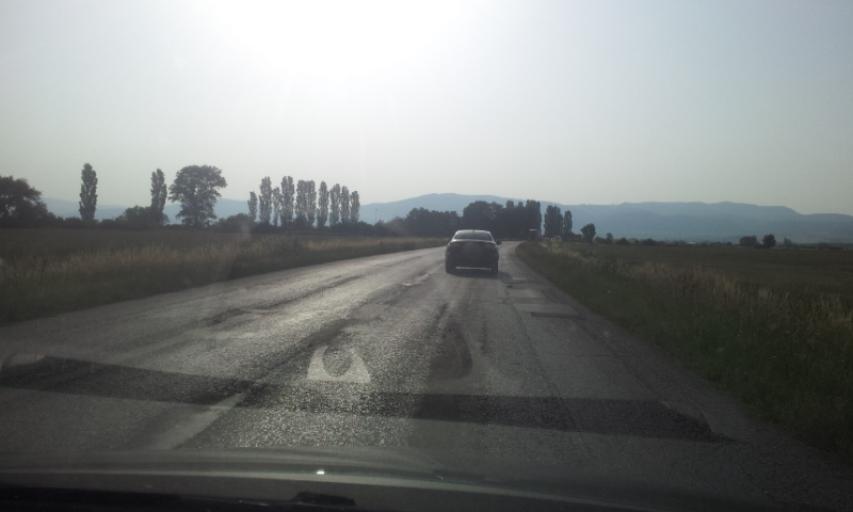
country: SK
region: Kosicky
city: Kosice
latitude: 48.6139
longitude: 21.2723
